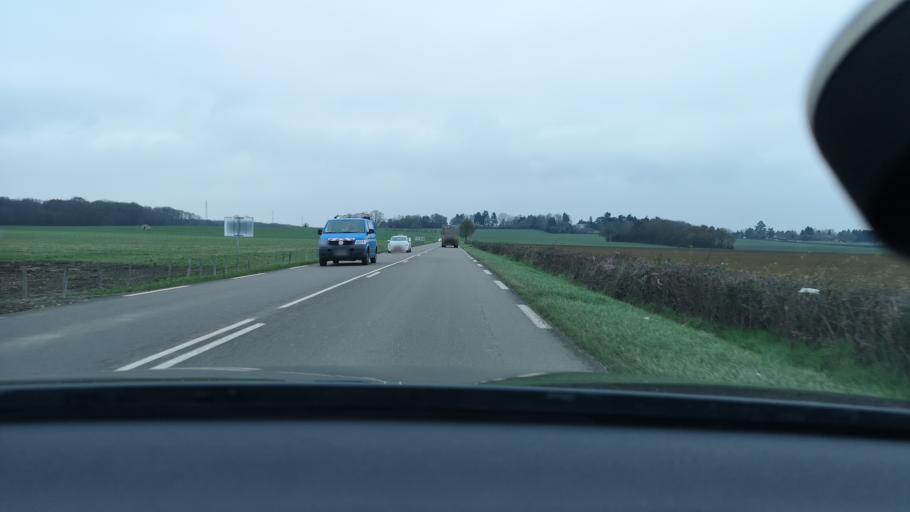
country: FR
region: Bourgogne
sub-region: Departement de Saone-et-Loire
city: Dracy-le-Fort
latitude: 46.8120
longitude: 4.7592
